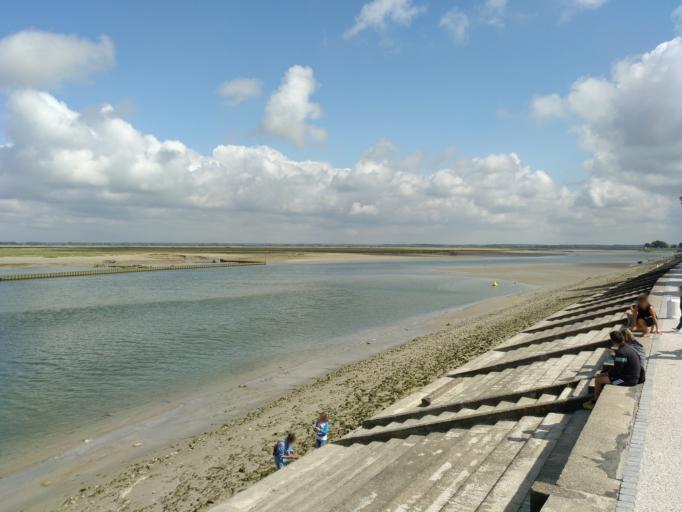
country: FR
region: Picardie
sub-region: Departement de la Somme
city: Saint-Valery-sur-Somme
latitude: 50.1903
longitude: 1.6271
